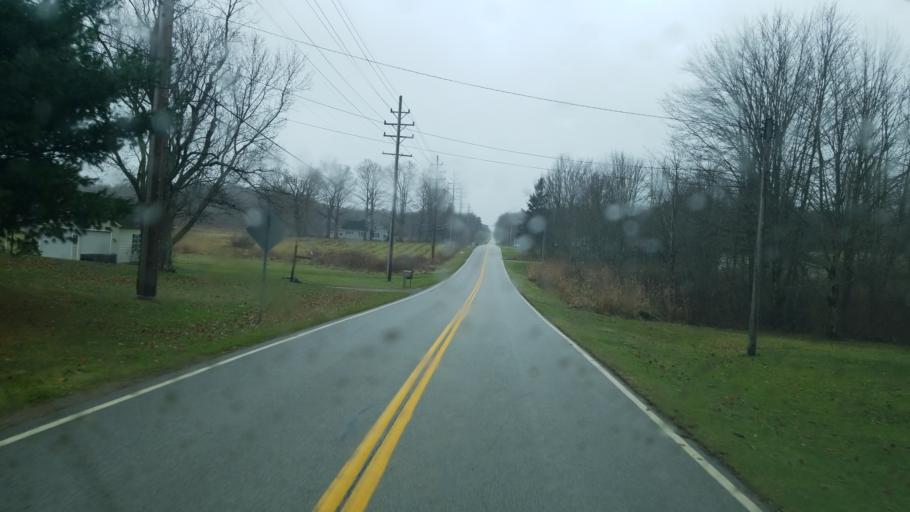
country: US
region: Ohio
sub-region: Ashtabula County
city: Ashtabula
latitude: 41.8106
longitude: -80.8094
